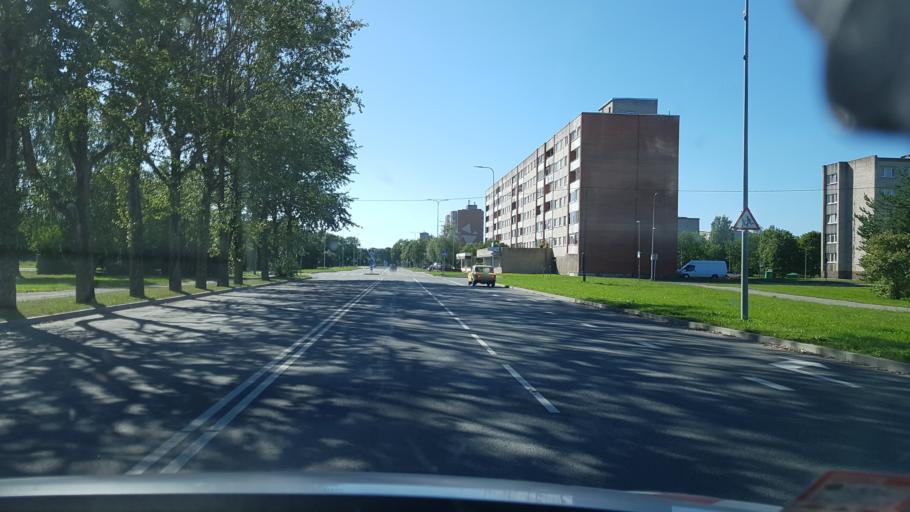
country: EE
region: Ida-Virumaa
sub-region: Kivioli linn
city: Kivioli
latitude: 59.3589
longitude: 26.9812
